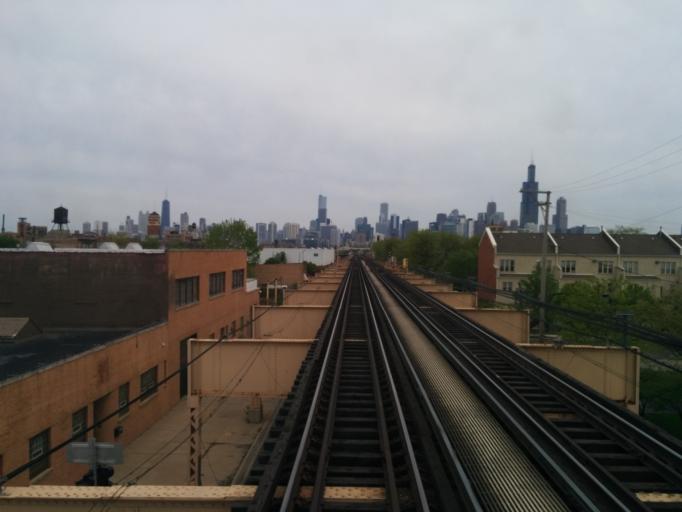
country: US
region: Illinois
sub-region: Cook County
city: Chicago
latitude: 41.8852
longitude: -87.6716
